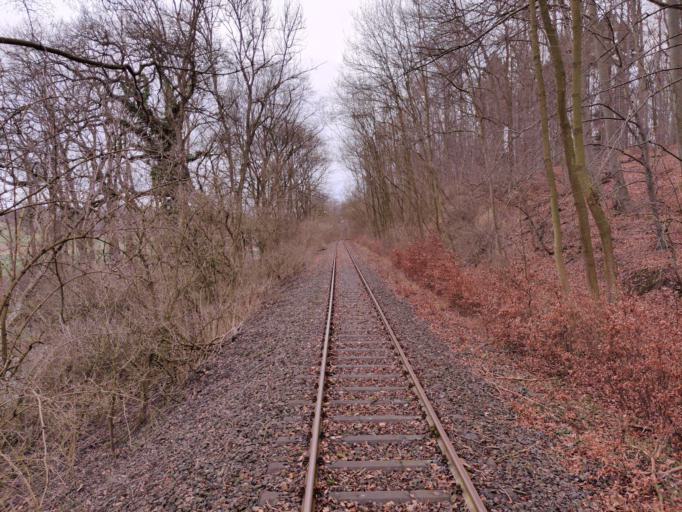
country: DE
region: Lower Saxony
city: Haverlah
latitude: 52.0642
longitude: 10.1389
